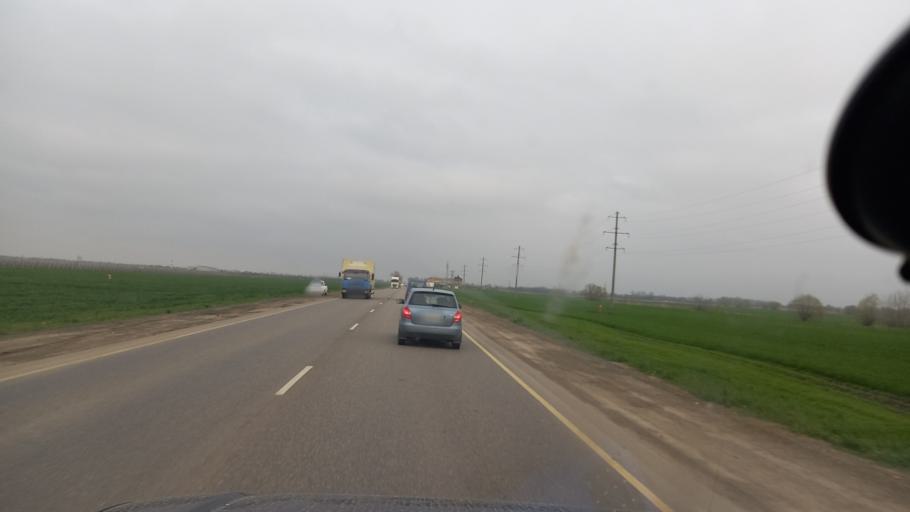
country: RU
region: Krasnodarskiy
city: Slavyansk-na-Kubani
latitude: 45.2414
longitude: 38.0278
